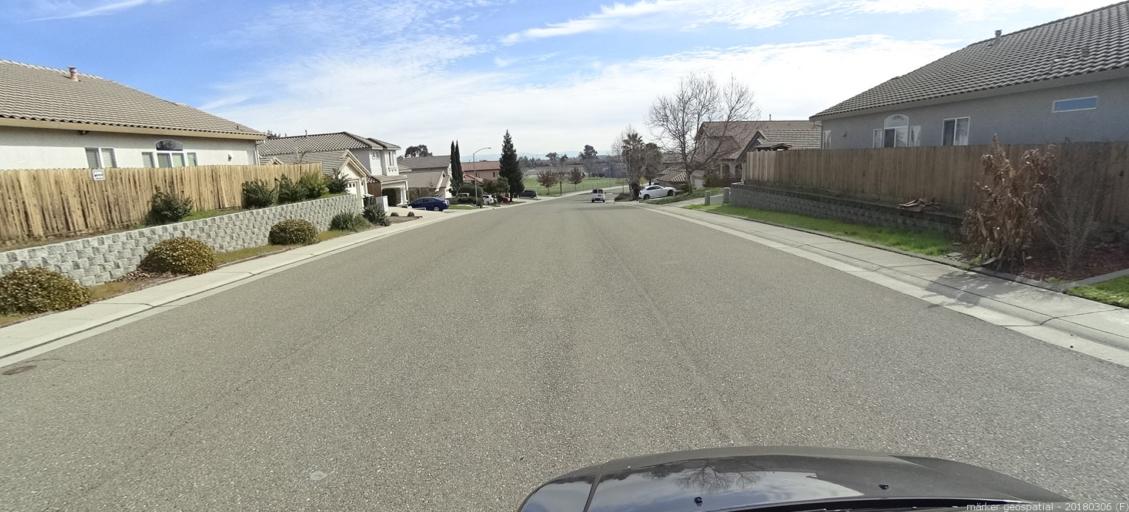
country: US
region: California
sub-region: Sacramento County
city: Vineyard
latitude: 38.4667
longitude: -121.3444
